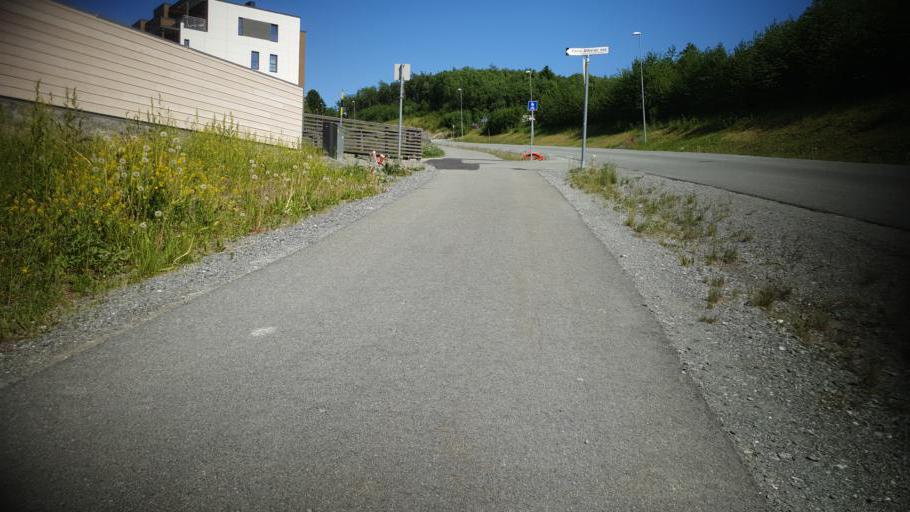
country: NO
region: Sor-Trondelag
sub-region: Malvik
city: Malvik
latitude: 63.4308
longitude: 10.5862
